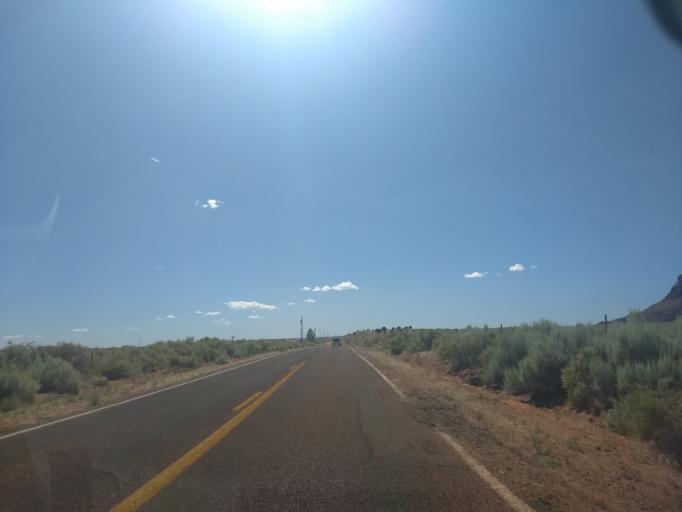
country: US
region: Arizona
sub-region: Mohave County
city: Colorado City
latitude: 36.9469
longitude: -112.9134
